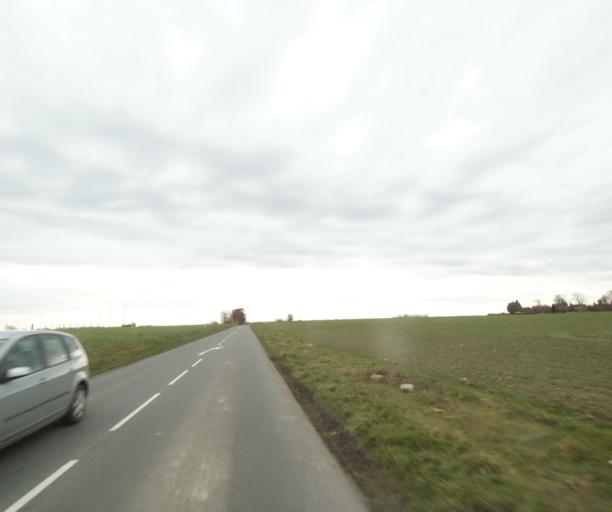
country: FR
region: Nord-Pas-de-Calais
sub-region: Departement du Nord
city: Curgies
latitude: 50.3575
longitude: 3.5969
